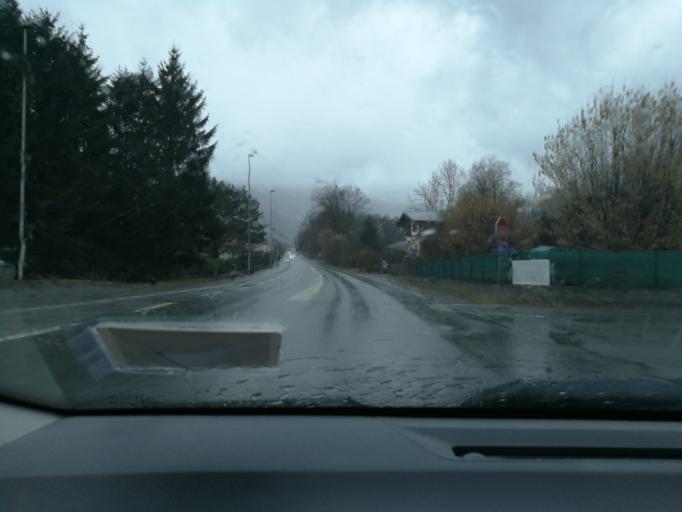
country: FR
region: Rhone-Alpes
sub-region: Departement de la Haute-Savoie
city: Domancy
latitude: 45.9320
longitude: 6.6522
